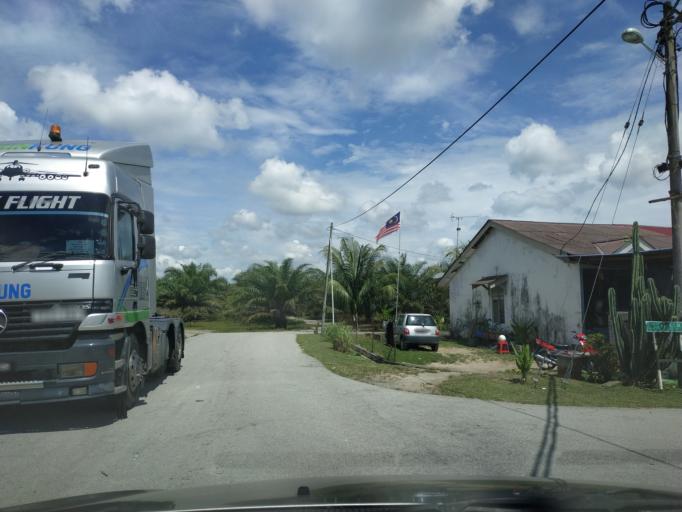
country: MY
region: Perak
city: Parit Buntar
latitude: 5.1398
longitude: 100.5933
